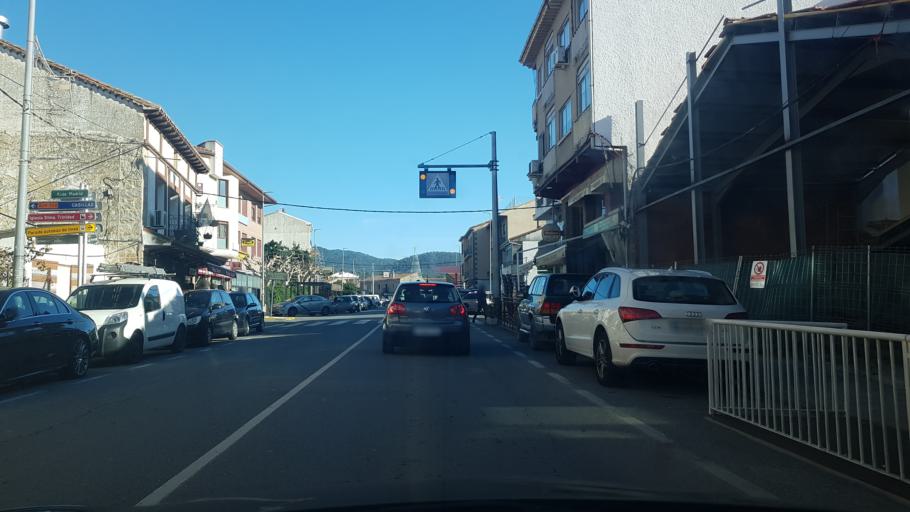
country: ES
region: Castille and Leon
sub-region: Provincia de Avila
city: Sotillo de la Adrada
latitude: 40.2936
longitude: -4.5809
